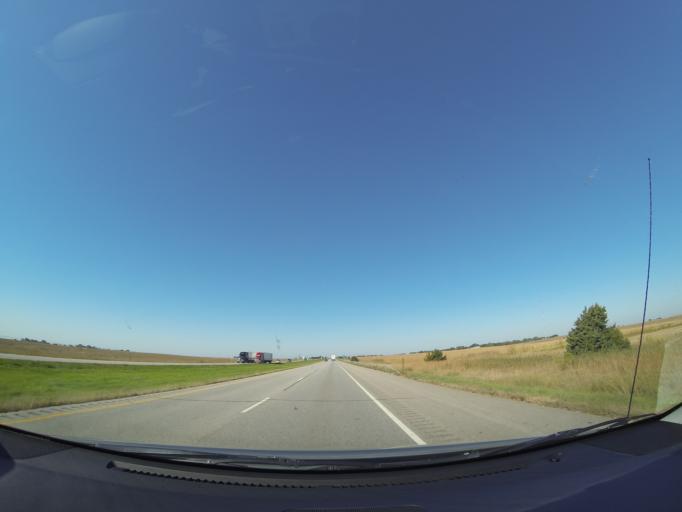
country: US
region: Nebraska
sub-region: Seward County
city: Seward
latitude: 40.8226
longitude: -97.1865
